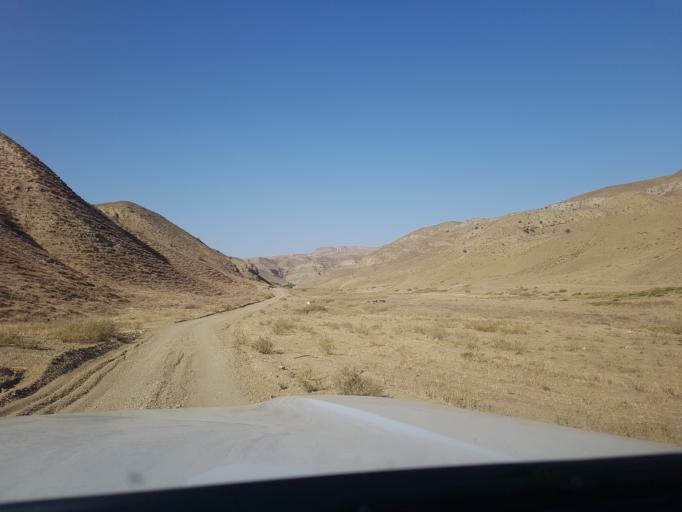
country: TM
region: Balkan
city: Magtymguly
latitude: 38.3012
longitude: 56.7668
